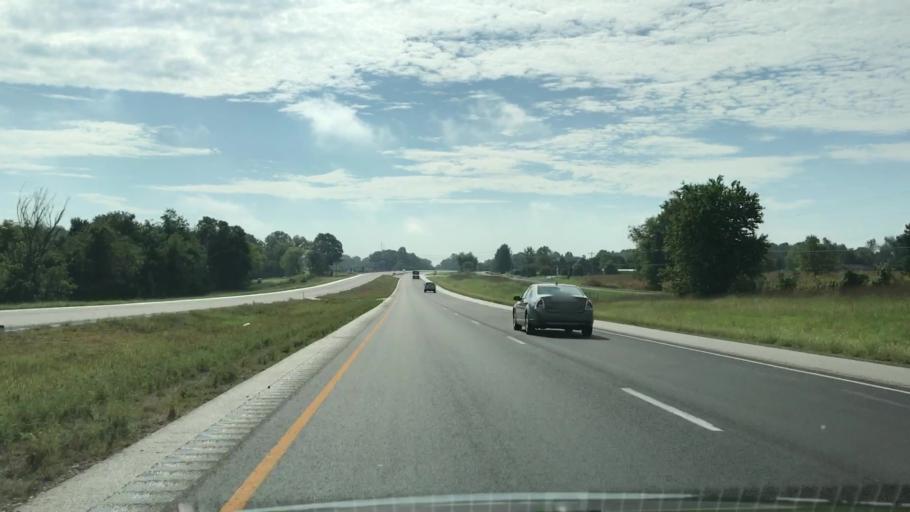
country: US
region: Kentucky
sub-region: Warren County
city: Plano
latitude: 36.8838
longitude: -86.3636
